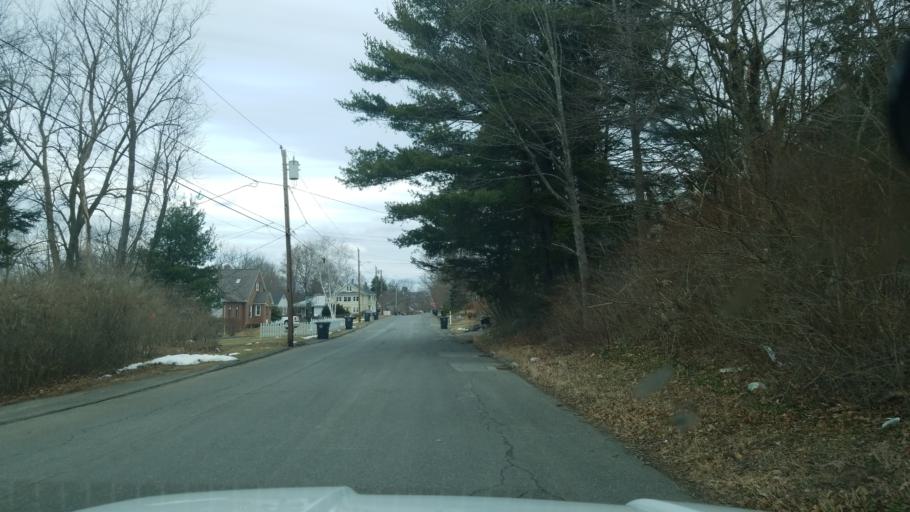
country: US
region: Connecticut
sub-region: Litchfield County
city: Torrington
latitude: 41.7970
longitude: -73.1047
